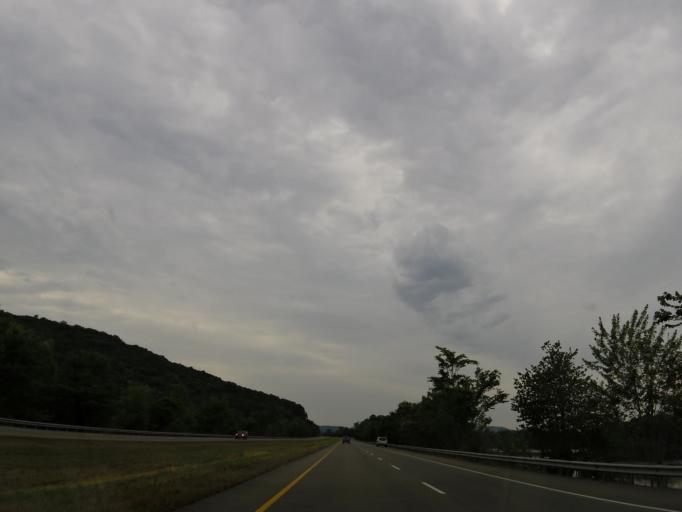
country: US
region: Alabama
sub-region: Jackson County
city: Scottsboro
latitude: 34.6178
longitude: -86.1259
